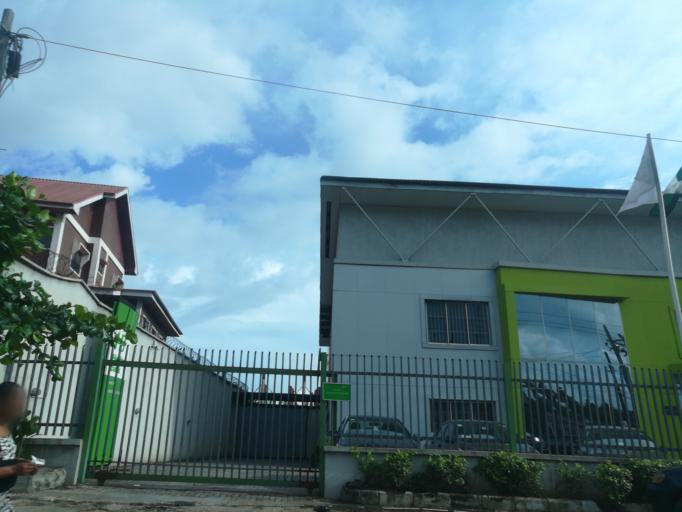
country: NG
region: Lagos
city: Ikeja
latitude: 6.6206
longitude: 3.3541
